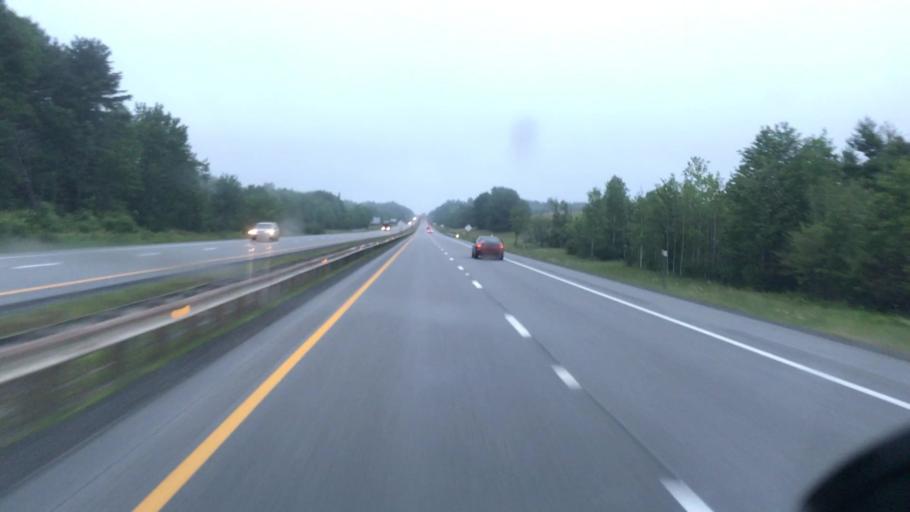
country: US
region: Maine
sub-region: Cumberland County
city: New Gloucester
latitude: 43.9081
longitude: -70.3399
